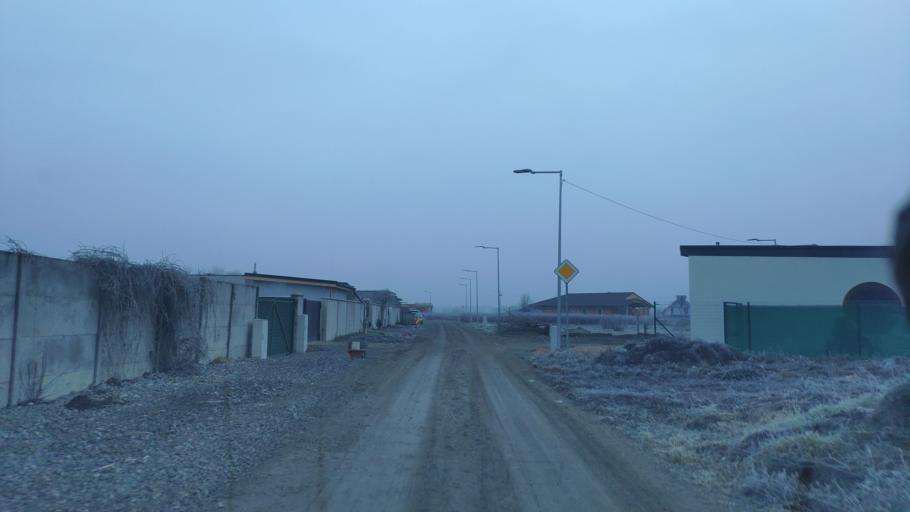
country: SK
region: Kosicky
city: Kosice
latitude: 48.6160
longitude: 21.3288
